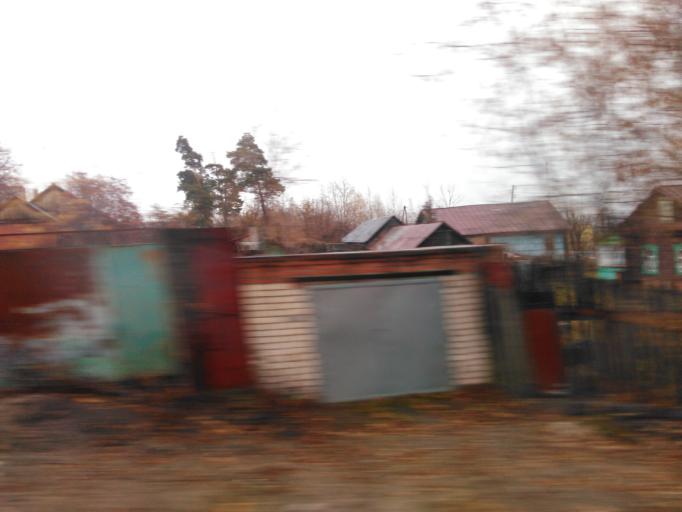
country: RU
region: Tatarstan
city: Osinovo
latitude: 55.8185
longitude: 48.8727
